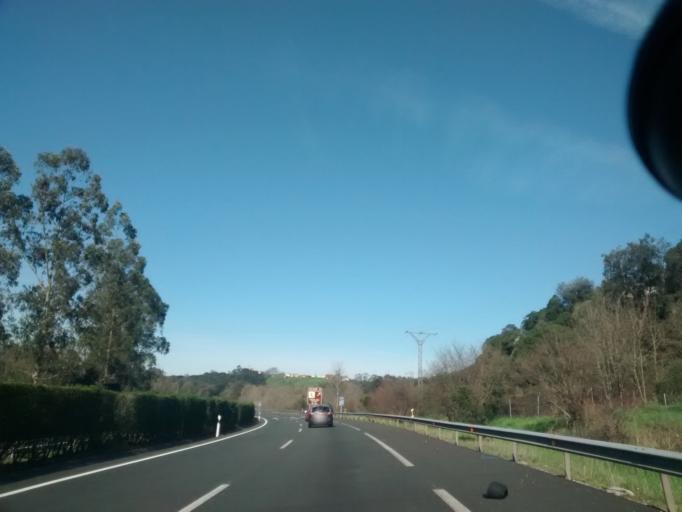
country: ES
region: Cantabria
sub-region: Provincia de Cantabria
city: Entrambasaguas
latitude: 43.3917
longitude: -3.6971
